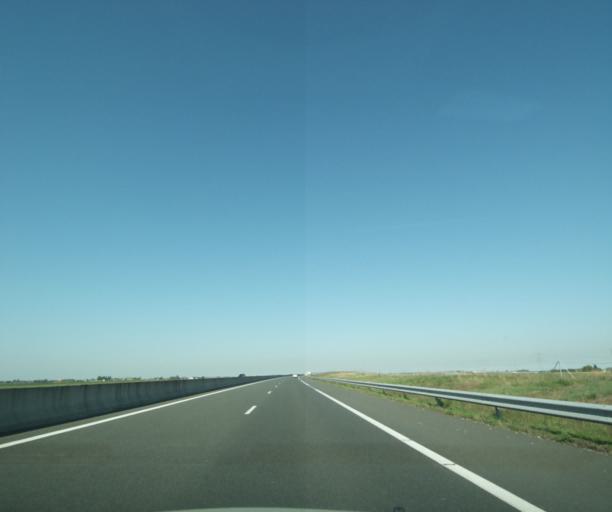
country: FR
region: Centre
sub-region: Departement du Loiret
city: Pithiviers-le-Vieil
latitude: 48.1119
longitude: 2.2199
